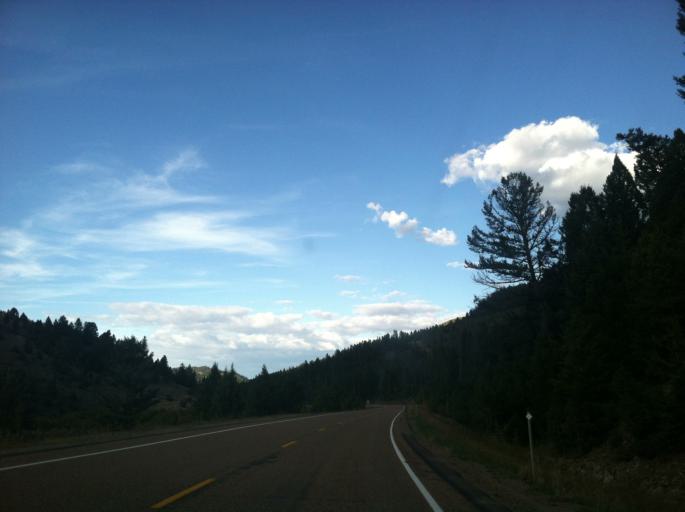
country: US
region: Montana
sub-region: Granite County
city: Philipsburg
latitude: 46.4225
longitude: -113.2783
